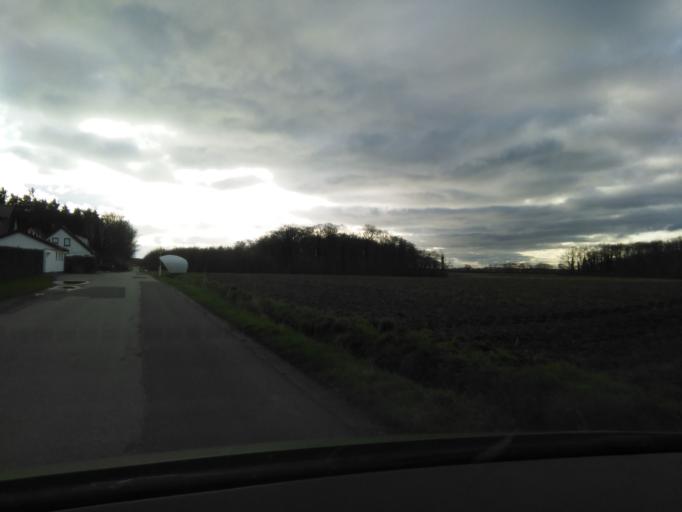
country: DK
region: Central Jutland
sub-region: Odder Kommune
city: Odder
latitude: 55.8730
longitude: 10.1698
